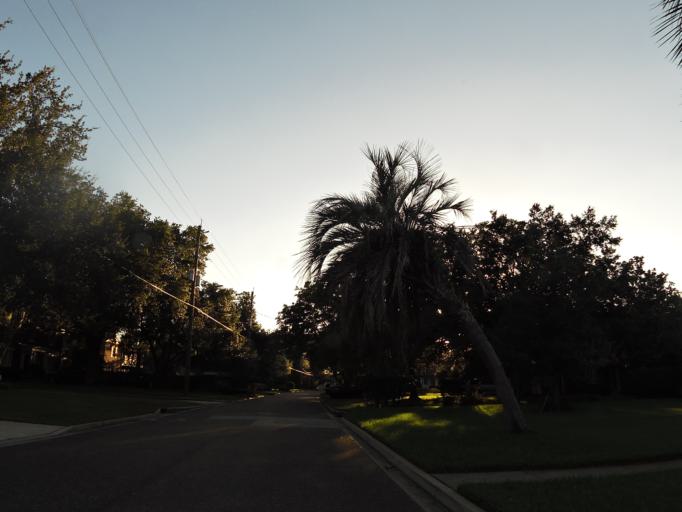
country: US
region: Florida
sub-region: Duval County
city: Jacksonville
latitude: 30.2983
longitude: -81.6511
